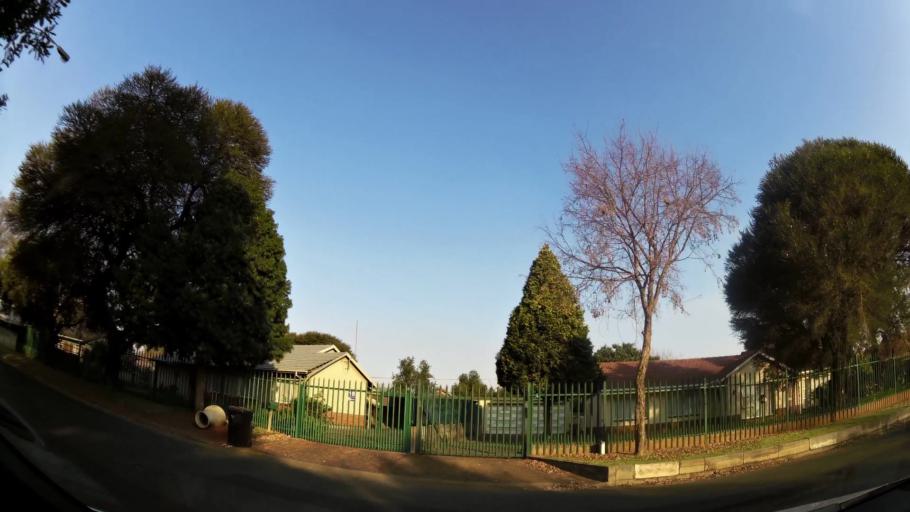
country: ZA
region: Gauteng
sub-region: Ekurhuleni Metropolitan Municipality
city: Springs
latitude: -26.2575
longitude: 28.3967
